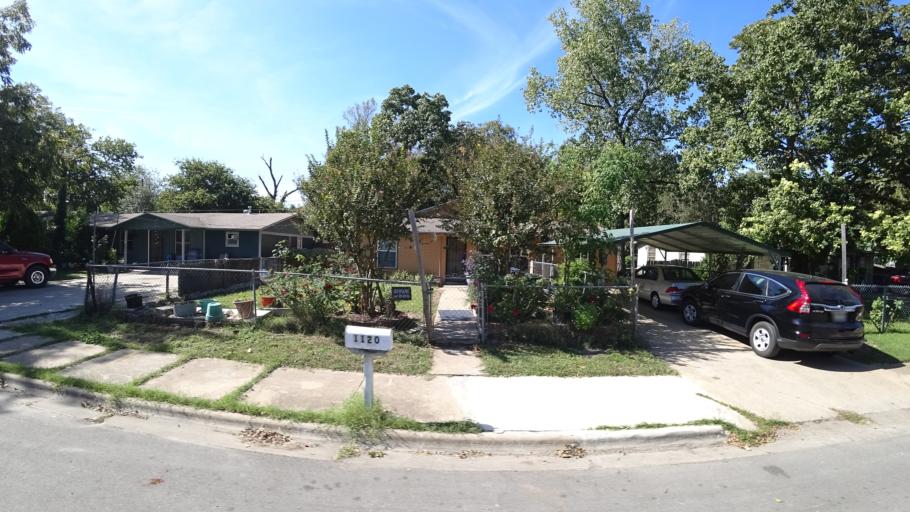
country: US
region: Texas
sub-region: Travis County
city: Austin
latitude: 30.2709
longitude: -97.6884
